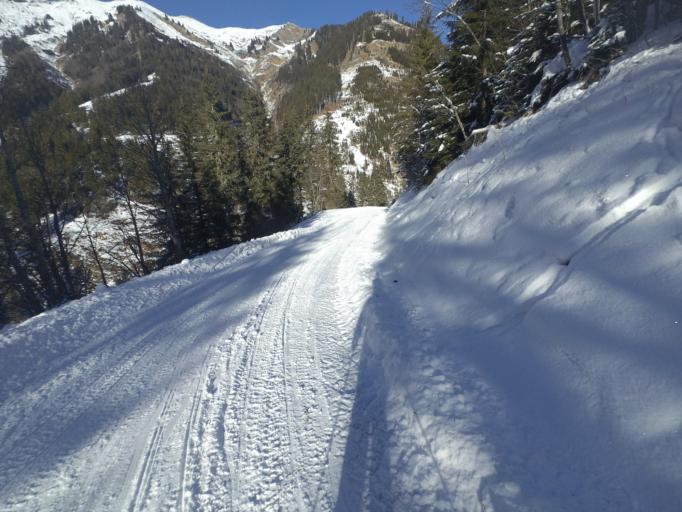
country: AT
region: Salzburg
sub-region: Politischer Bezirk Sankt Johann im Pongau
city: Huttschlag
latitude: 47.1807
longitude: 13.2701
